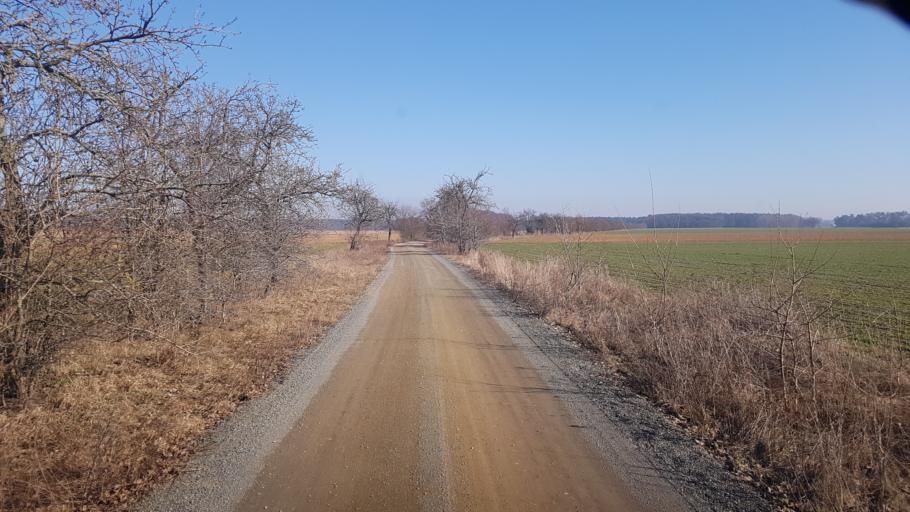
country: DE
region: Brandenburg
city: Ihlow
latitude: 51.8225
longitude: 13.3606
